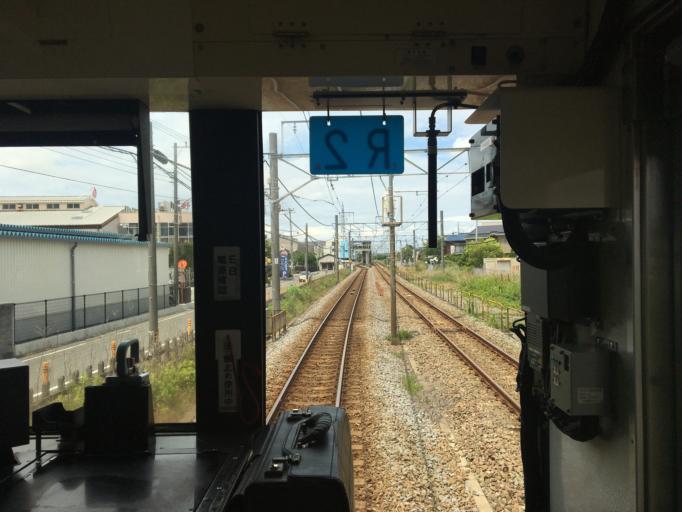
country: JP
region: Kanagawa
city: Chigasaki
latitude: 35.3375
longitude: 139.4086
